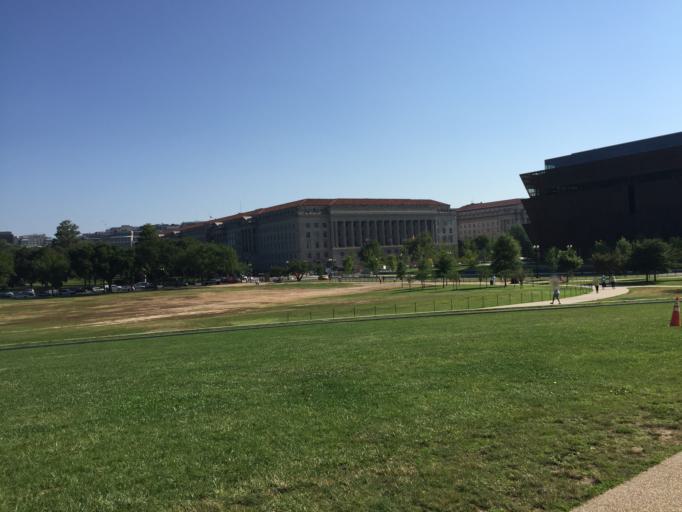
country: US
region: Washington, D.C.
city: Washington, D.C.
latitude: 38.8902
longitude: -77.0348
